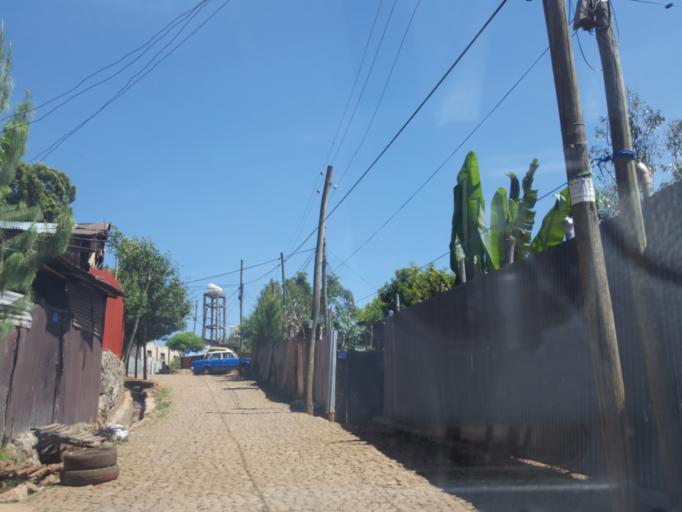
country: ET
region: Adis Abeba
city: Addis Ababa
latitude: 9.0638
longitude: 38.7465
